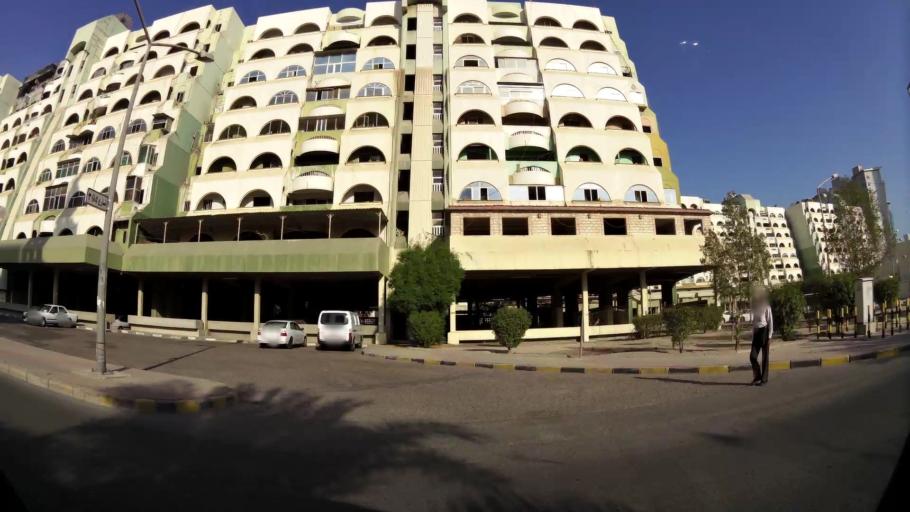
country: KW
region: Al Asimah
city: Kuwait City
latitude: 29.3745
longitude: 47.9840
